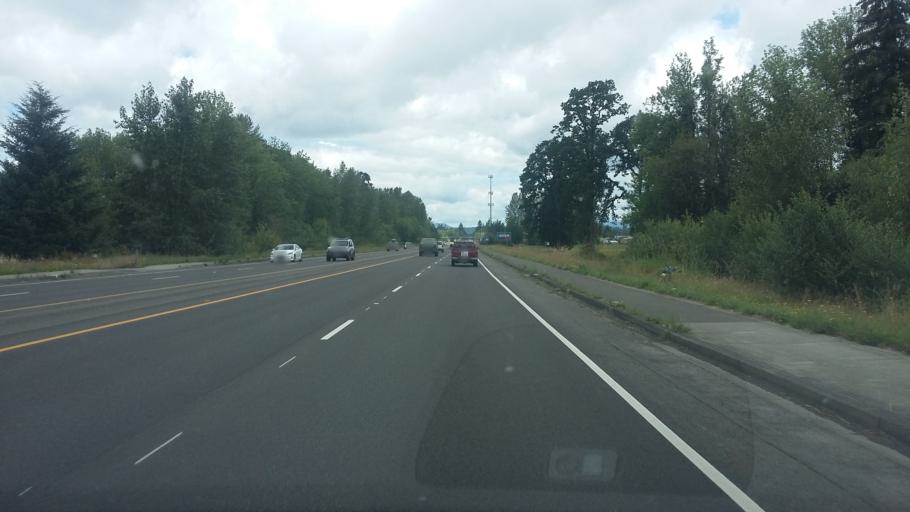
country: US
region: Washington
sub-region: Clark County
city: Battle Ground
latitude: 45.7727
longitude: -122.5474
